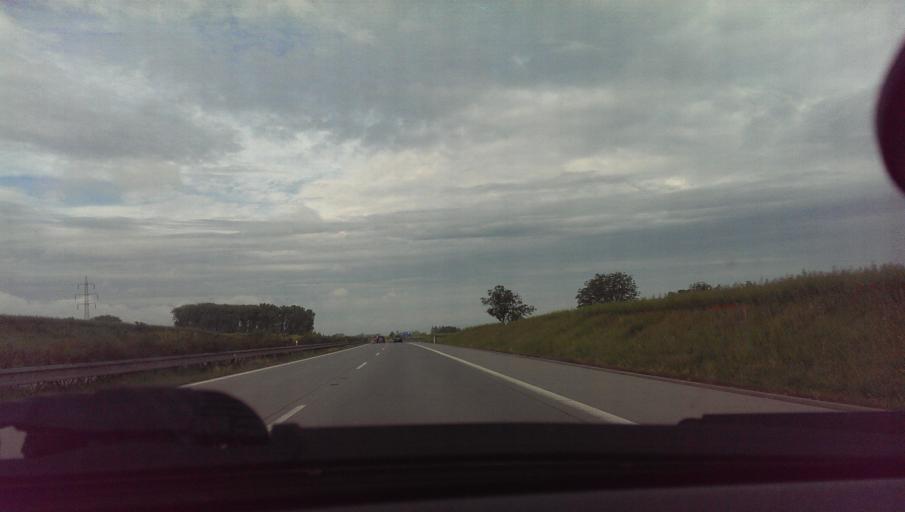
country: CZ
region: Olomoucky
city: Kojetin
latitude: 49.3230
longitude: 17.2984
